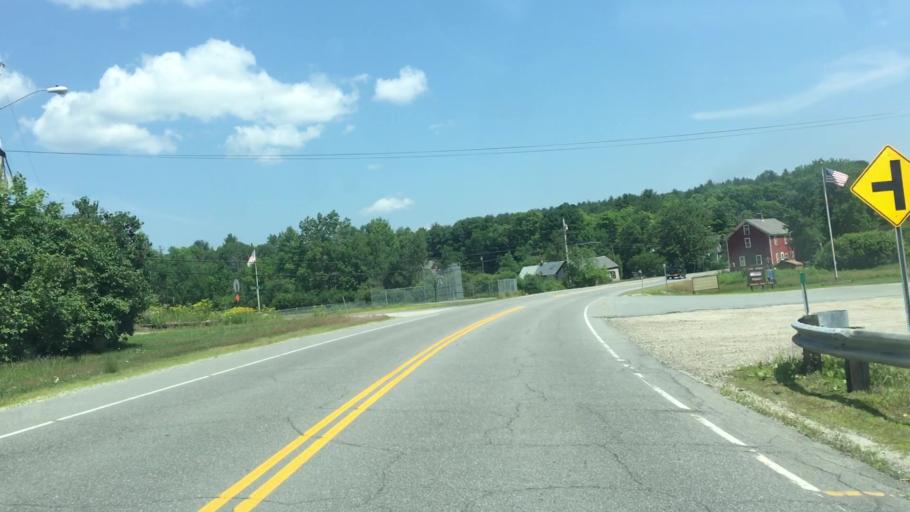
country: US
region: New Hampshire
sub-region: Sullivan County
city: Grantham
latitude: 43.4503
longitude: -72.1621
